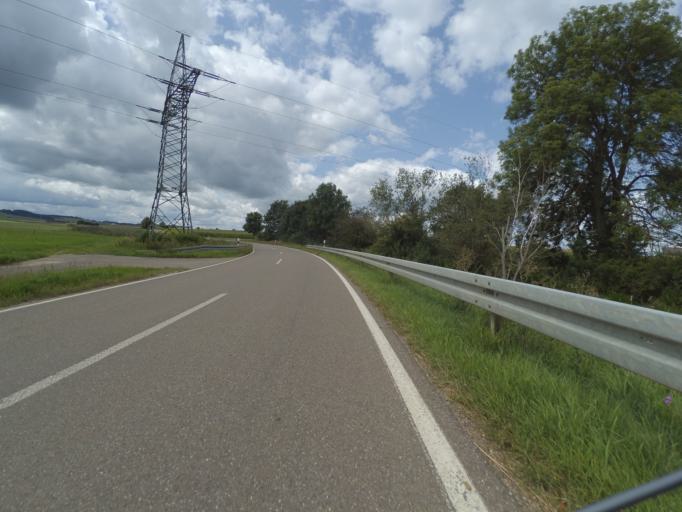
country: DE
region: Baden-Wuerttemberg
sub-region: Freiburg Region
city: Hufingen
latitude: 47.9100
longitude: 8.5613
